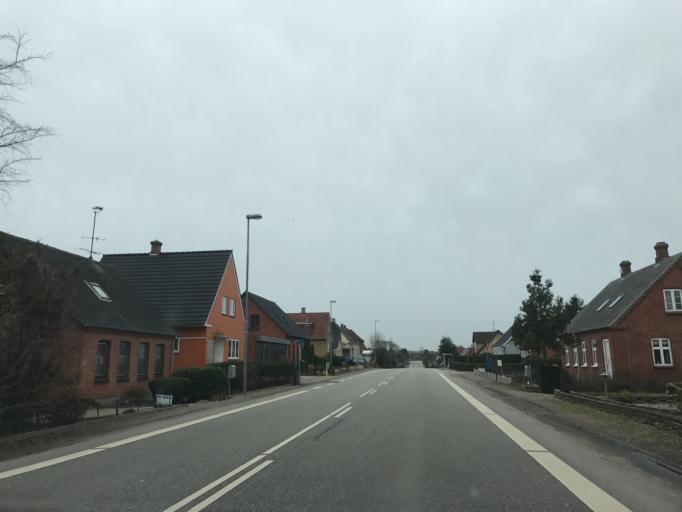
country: DK
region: South Denmark
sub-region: Langeland Kommune
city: Rudkobing
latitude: 54.9581
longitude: 10.7998
